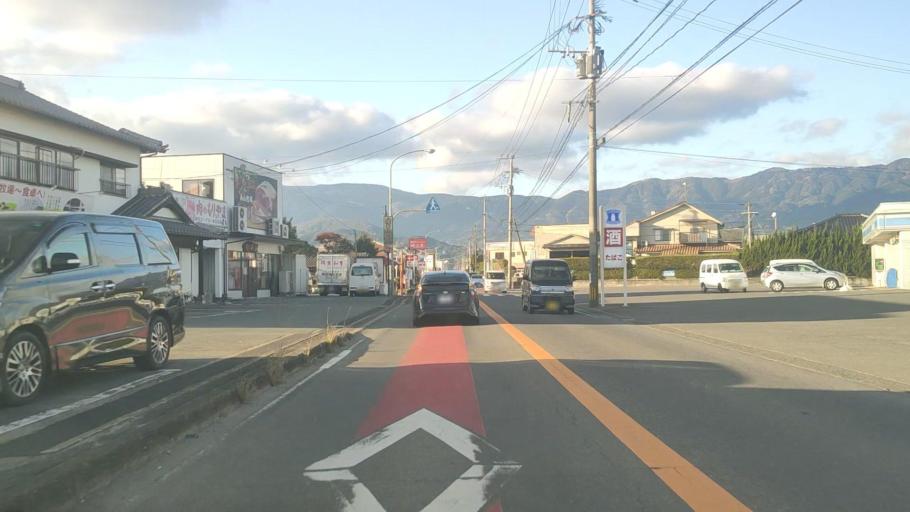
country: JP
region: Saga Prefecture
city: Saga-shi
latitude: 33.2811
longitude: 130.2121
